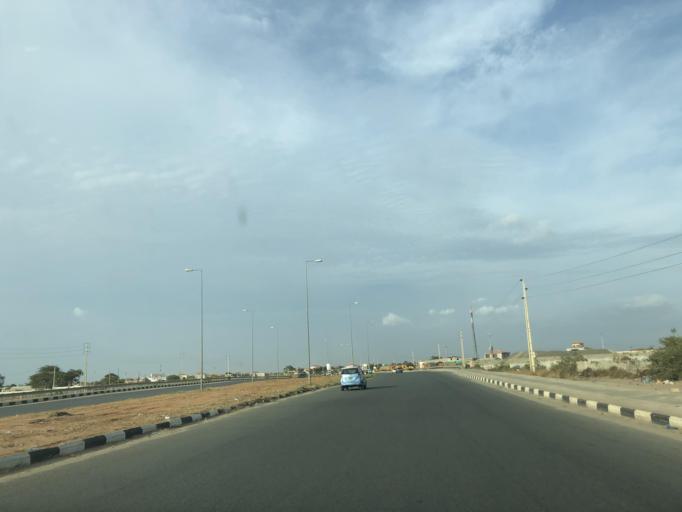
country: AO
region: Luanda
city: Luanda
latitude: -8.9349
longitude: 13.2989
